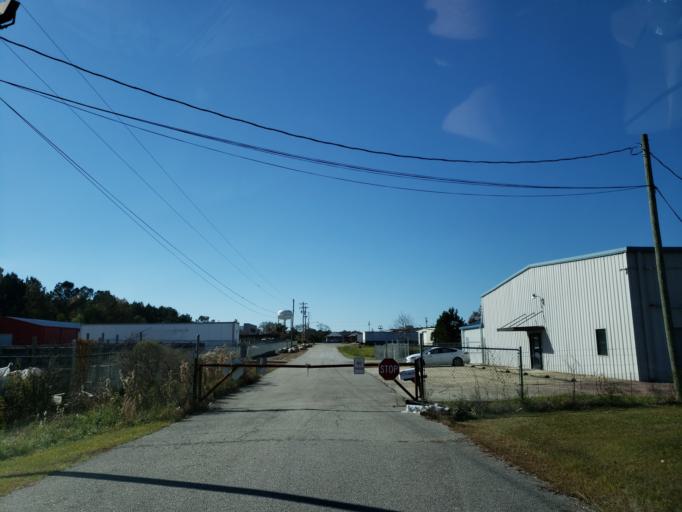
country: US
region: Mississippi
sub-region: Lamar County
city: West Hattiesburg
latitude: 31.3162
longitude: -89.4030
